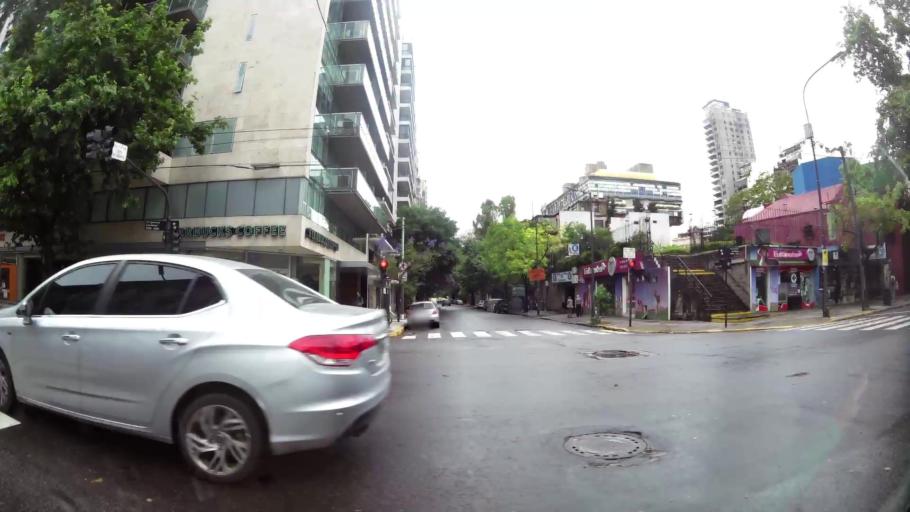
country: AR
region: Buenos Aires F.D.
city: Retiro
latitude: -34.5851
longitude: -58.3999
